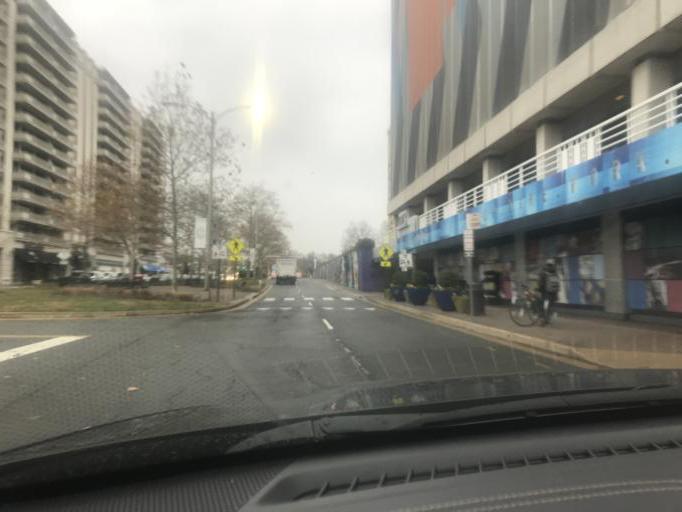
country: US
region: Washington, D.C.
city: Washington, D.C.
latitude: 38.8534
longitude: -77.0500
